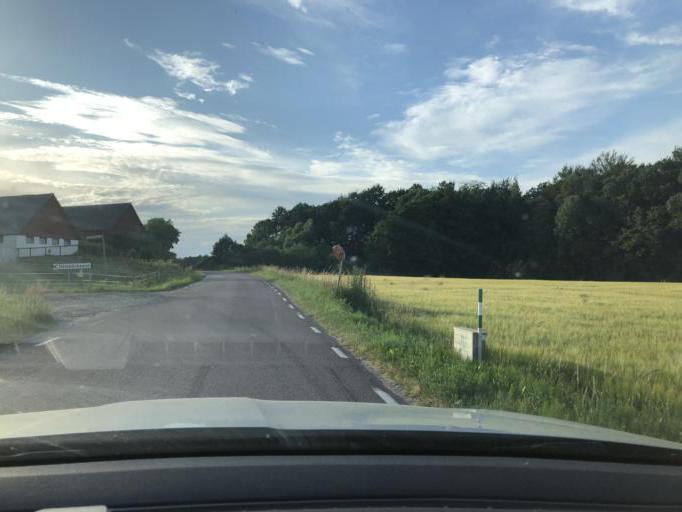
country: SE
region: Blekinge
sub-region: Solvesborgs Kommun
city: Soelvesborg
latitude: 56.1186
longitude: 14.6210
